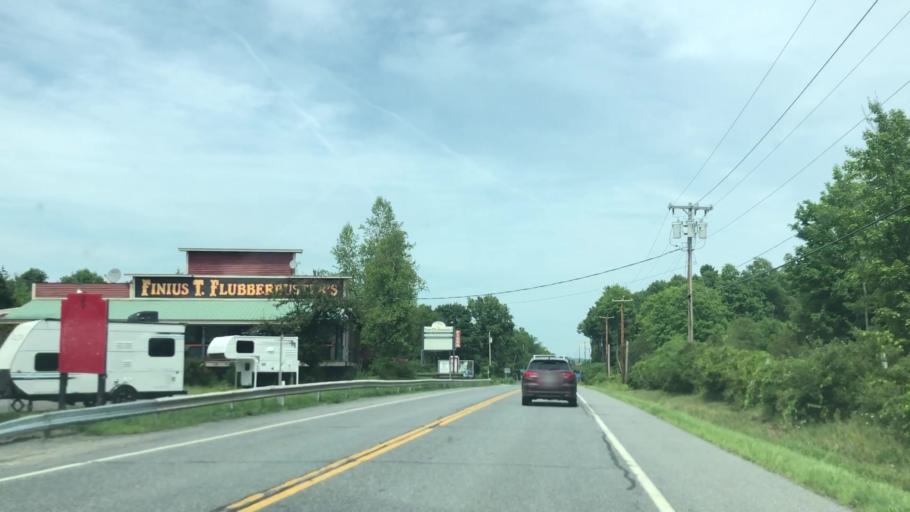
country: US
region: Vermont
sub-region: Rutland County
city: Fair Haven
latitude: 43.5746
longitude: -73.3117
